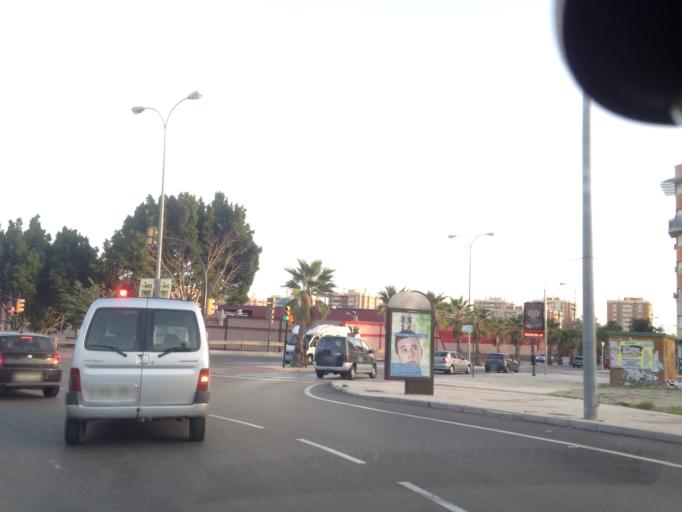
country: ES
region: Andalusia
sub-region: Provincia de Malaga
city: Malaga
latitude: 36.7362
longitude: -4.4335
